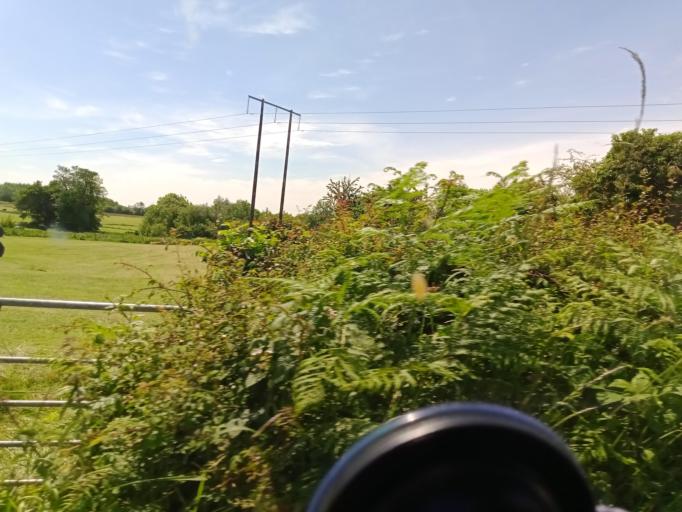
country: IE
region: Leinster
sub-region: Kilkenny
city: Thomastown
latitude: 52.5505
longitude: -7.0793
